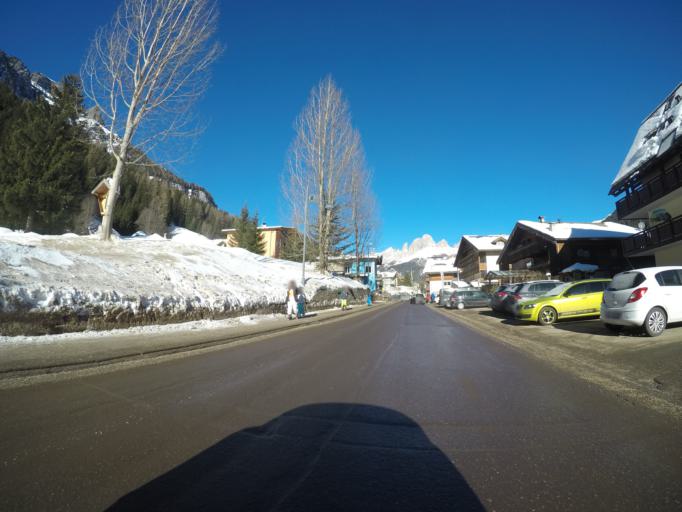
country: IT
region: Trentino-Alto Adige
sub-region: Provincia di Trento
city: Canazei
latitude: 46.4602
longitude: 11.7845
